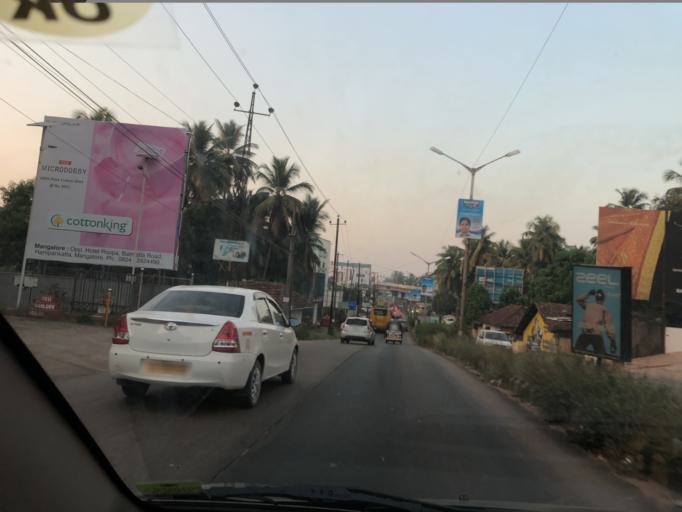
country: IN
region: Karnataka
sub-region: Dakshina Kannada
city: Mangalore
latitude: 12.9079
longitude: 74.8362
